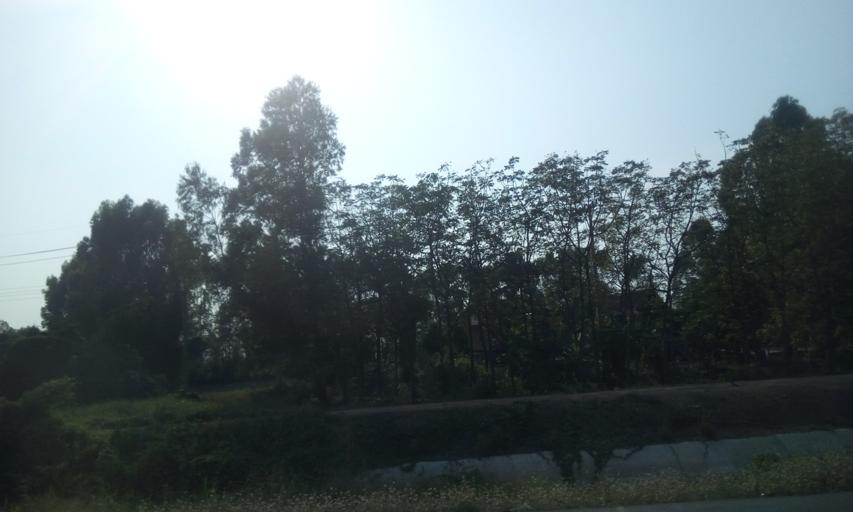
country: TH
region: Sing Buri
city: Phrom Buri
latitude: 14.7951
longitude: 100.4440
